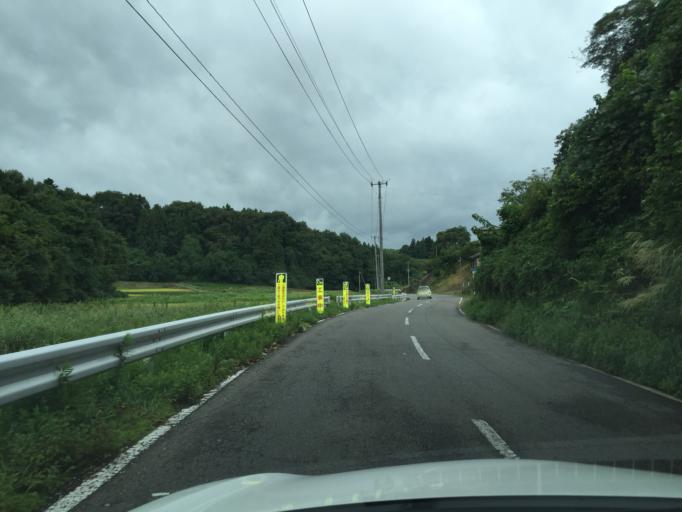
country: JP
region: Fukushima
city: Funehikimachi-funehiki
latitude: 37.4624
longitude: 140.5425
